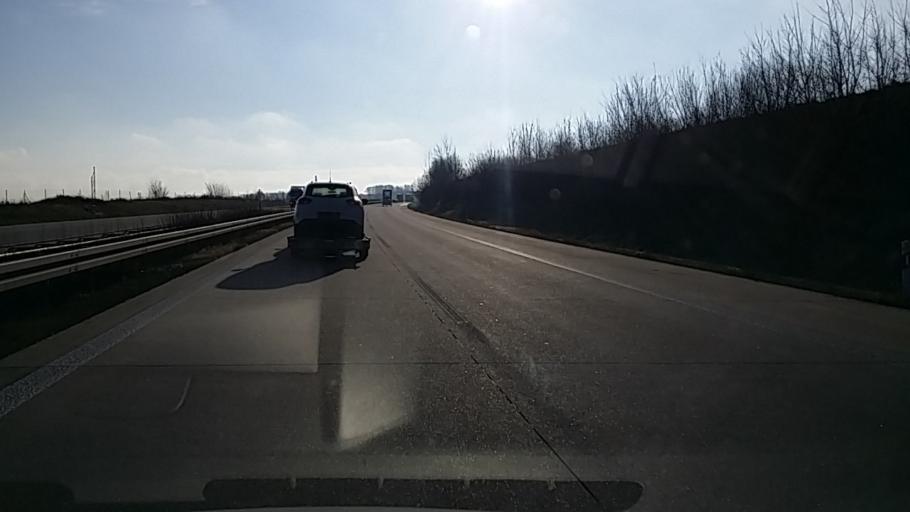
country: DE
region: Saxony
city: Dohna
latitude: 50.9294
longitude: 13.8893
